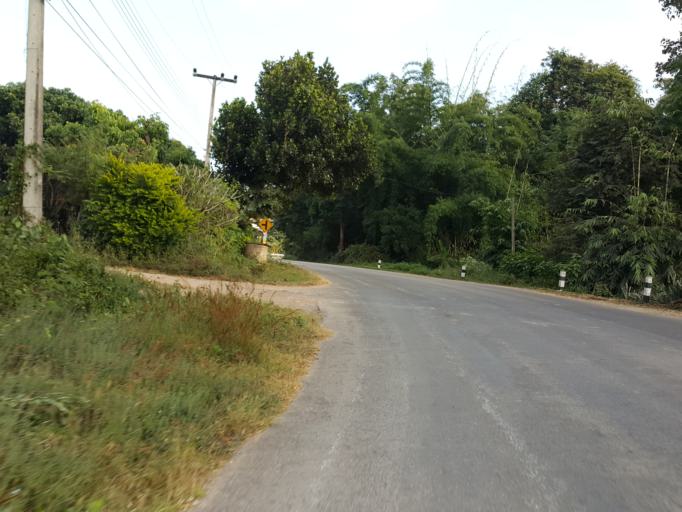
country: TH
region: Lamphun
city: Thung Hua Chang
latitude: 18.1245
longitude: 99.0134
